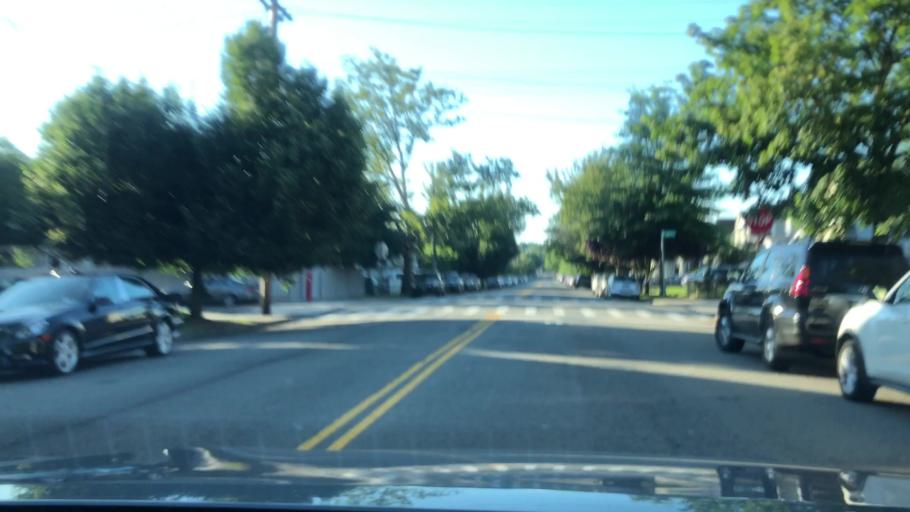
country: US
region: New York
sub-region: Nassau County
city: Bellerose Terrace
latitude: 40.7241
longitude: -73.7435
